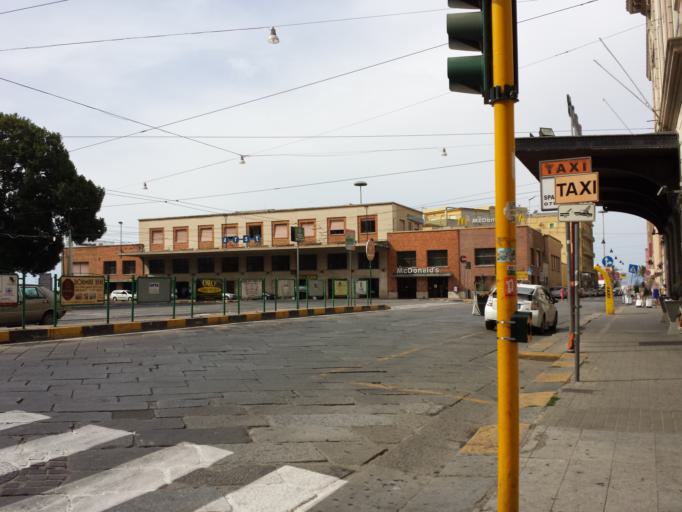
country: IT
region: Sardinia
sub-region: Provincia di Cagliari
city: Cagliari
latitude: 39.2157
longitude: 9.1093
